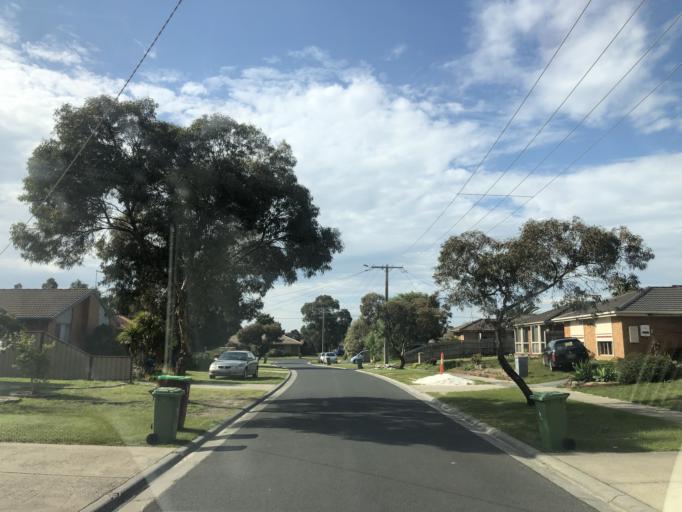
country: AU
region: Victoria
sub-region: Casey
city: Hampton Park
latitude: -38.0361
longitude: 145.2504
